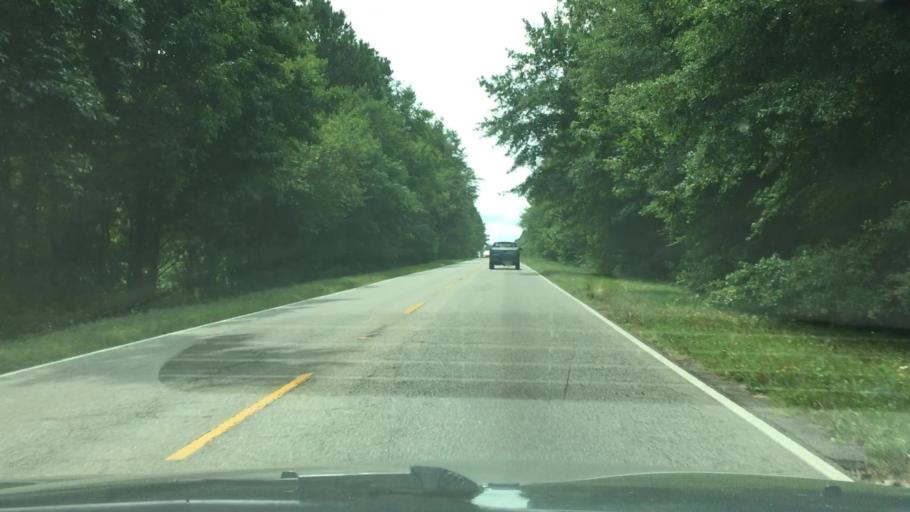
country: US
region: South Carolina
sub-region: Aiken County
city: Aiken
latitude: 33.5268
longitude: -81.7388
